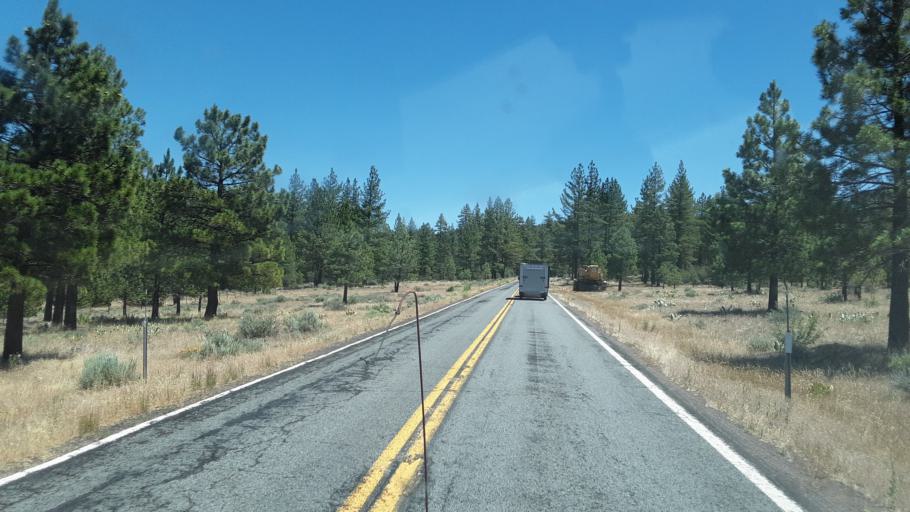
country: US
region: California
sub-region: Modoc County
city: Alturas
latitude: 40.9789
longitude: -120.7856
